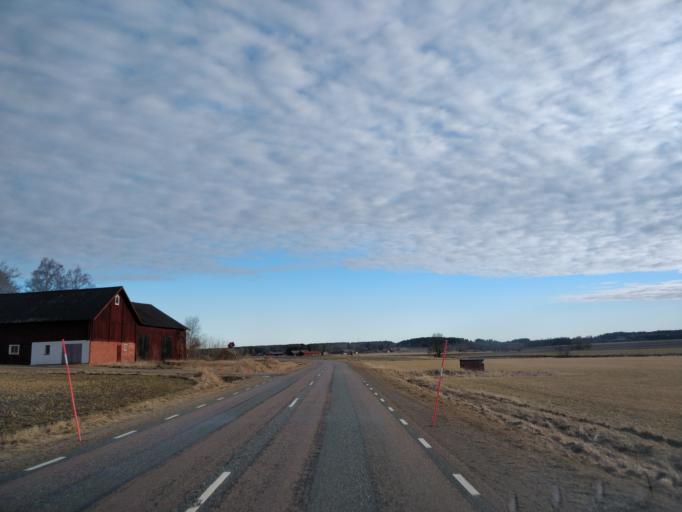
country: SE
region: Uppsala
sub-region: Enkopings Kommun
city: Enkoping
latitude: 59.7912
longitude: 17.0885
